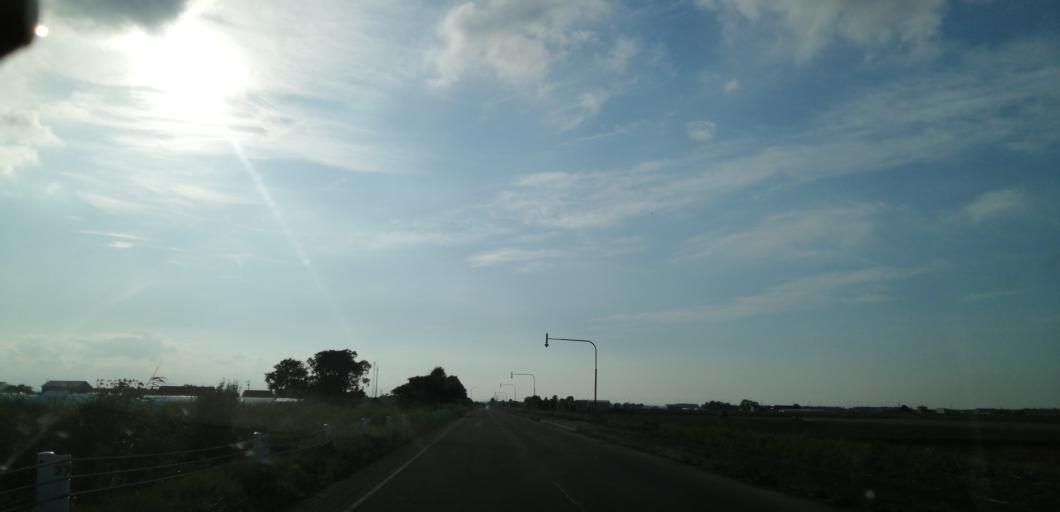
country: JP
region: Hokkaido
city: Kitahiroshima
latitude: 42.9446
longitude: 141.6836
